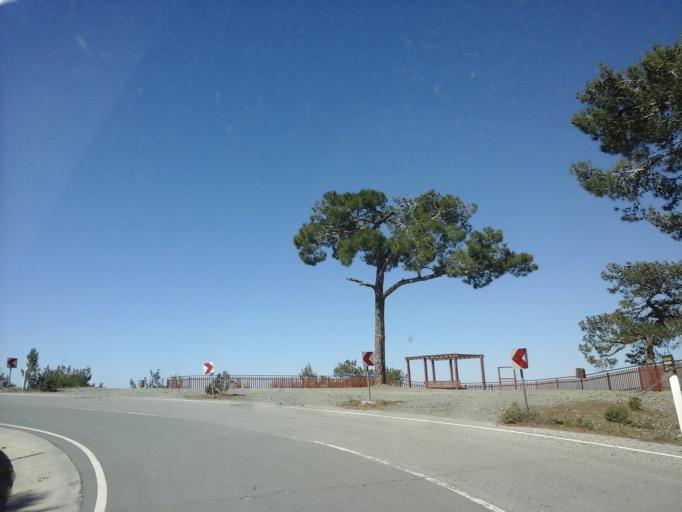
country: CY
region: Lefkosia
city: Kakopetria
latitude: 34.9155
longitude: 32.8302
